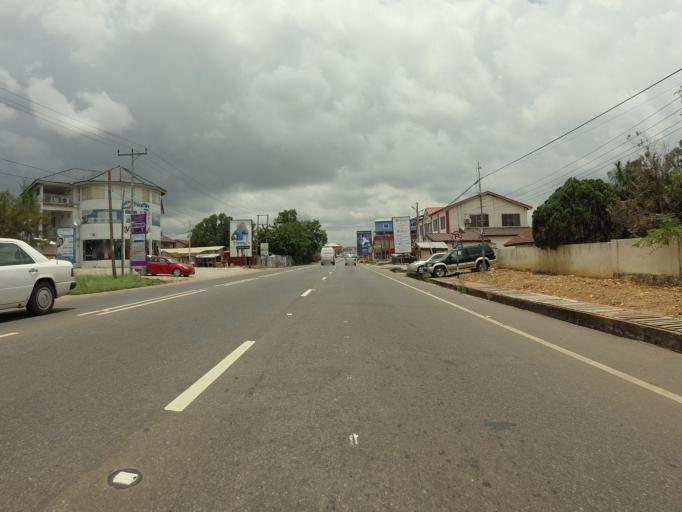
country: GH
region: Greater Accra
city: Medina Estates
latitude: 5.6413
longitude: -0.1461
